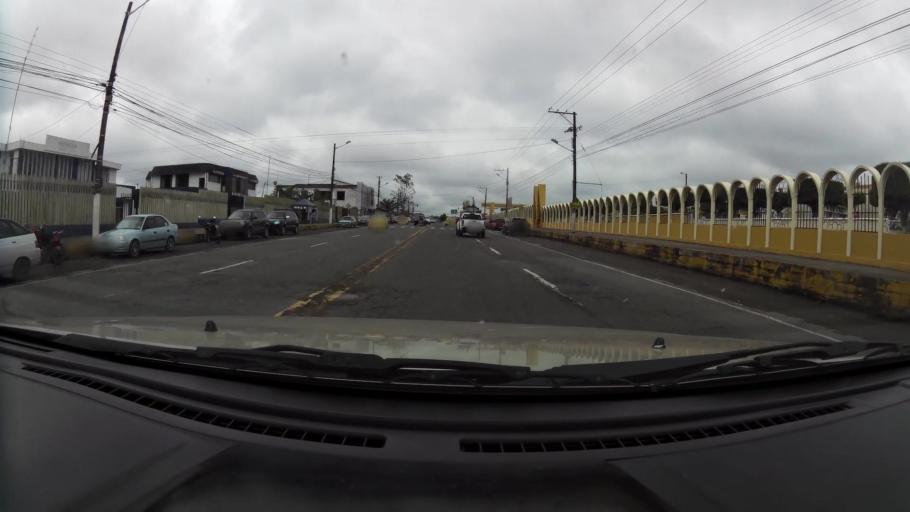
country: EC
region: Santo Domingo de los Tsachilas
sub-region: Canton Santo Domingo de los Colorados
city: Santo Domingo de los Colorados
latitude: -0.2414
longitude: -79.1682
